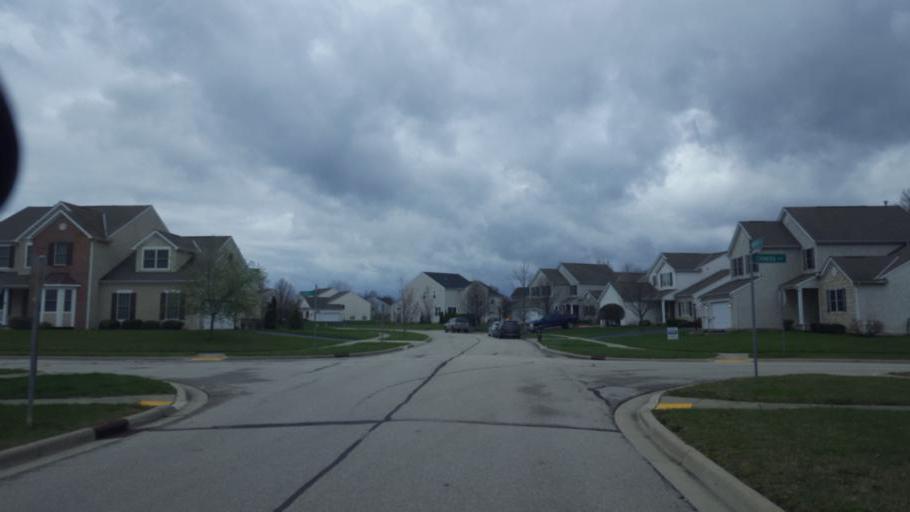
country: US
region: Ohio
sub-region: Franklin County
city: Westerville
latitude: 40.1867
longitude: -82.9050
